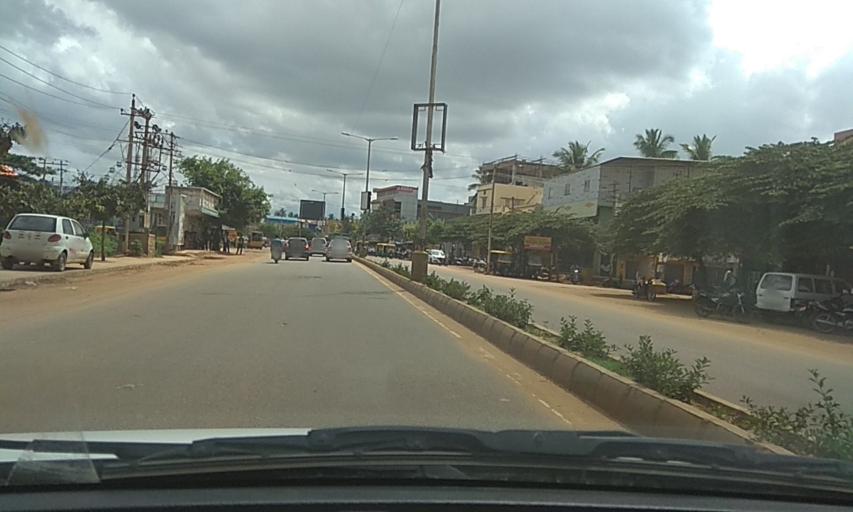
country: IN
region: Karnataka
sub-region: Tumkur
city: Tumkur
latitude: 13.3296
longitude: 77.0945
